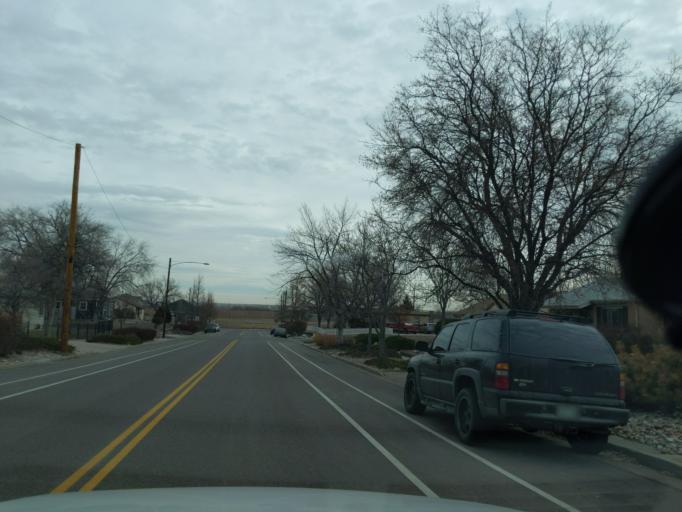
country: US
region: Colorado
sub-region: Adams County
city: Thornton
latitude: 39.8661
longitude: -104.9513
